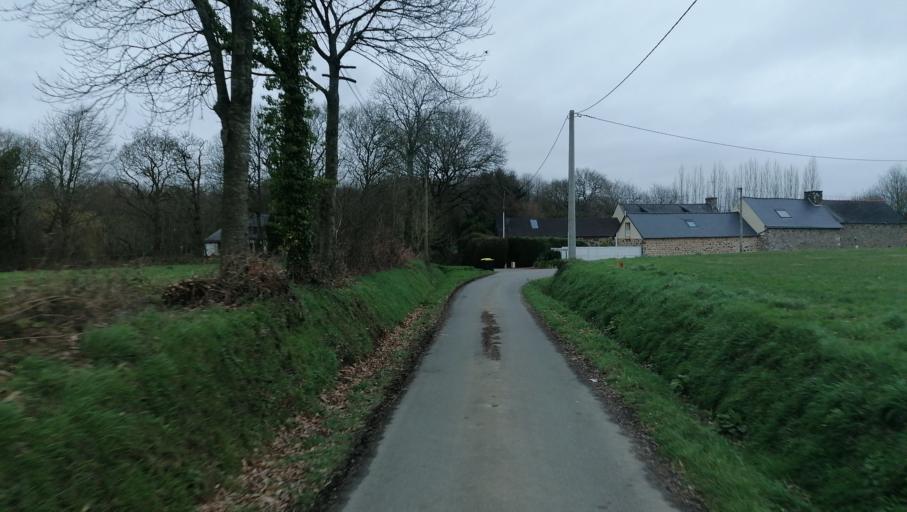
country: FR
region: Brittany
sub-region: Departement des Cotes-d'Armor
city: Saint-Agathon
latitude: 48.5743
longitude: -3.0636
